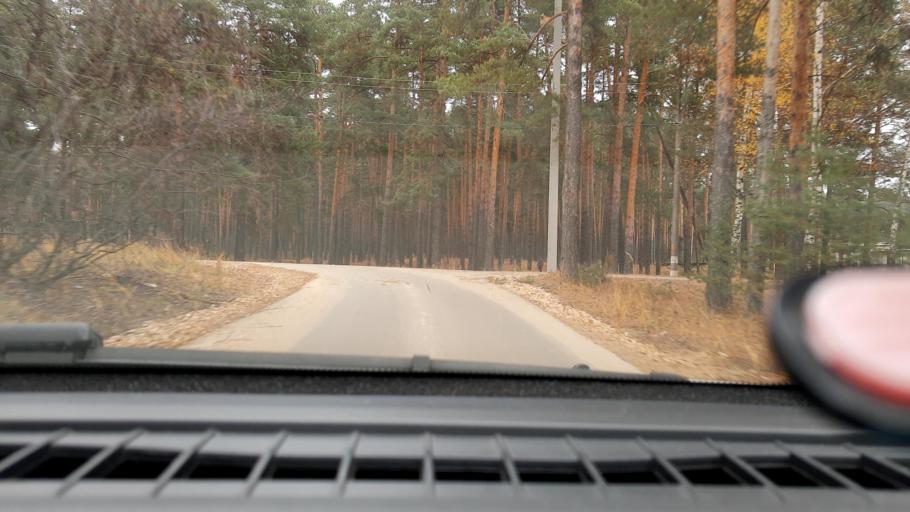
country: RU
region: Nizjnij Novgorod
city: Lukino
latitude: 56.3932
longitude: 43.7203
